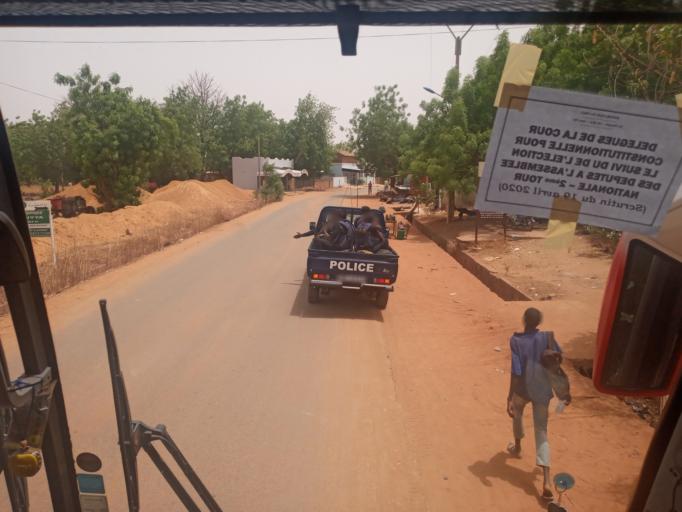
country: ML
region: Koulikoro
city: Koulikoro
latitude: 12.8942
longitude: -7.5403
